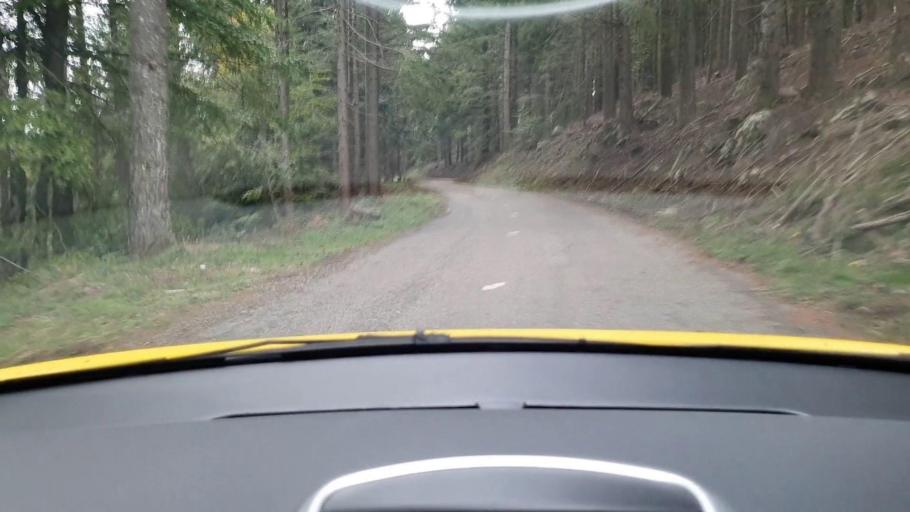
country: FR
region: Languedoc-Roussillon
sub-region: Departement de la Lozere
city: Meyrueis
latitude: 44.0908
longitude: 3.4563
